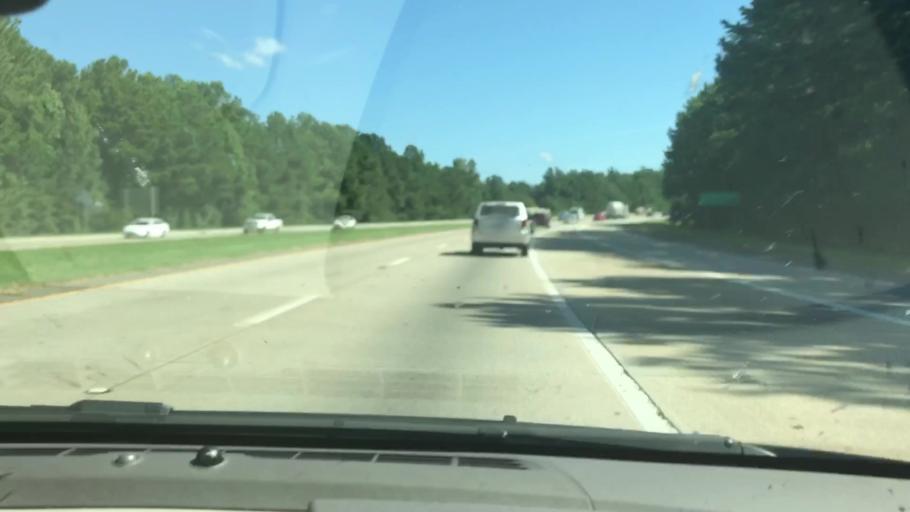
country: US
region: Alabama
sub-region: Russell County
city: Phenix City
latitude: 32.5377
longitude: -84.9734
